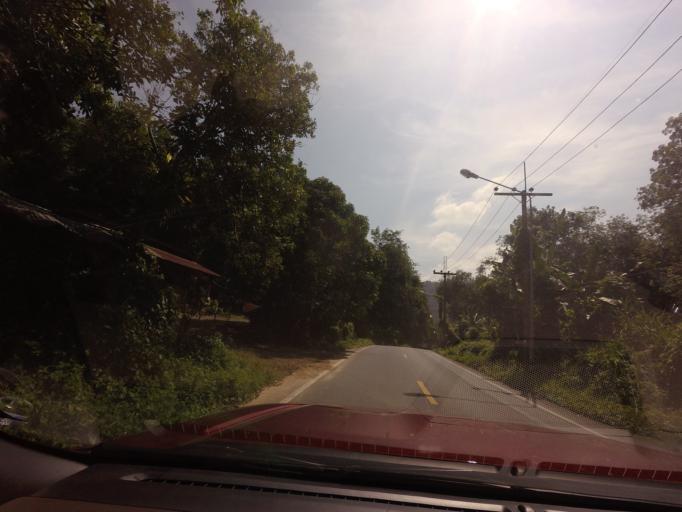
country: TH
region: Yala
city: Betong
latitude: 5.8236
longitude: 101.0760
